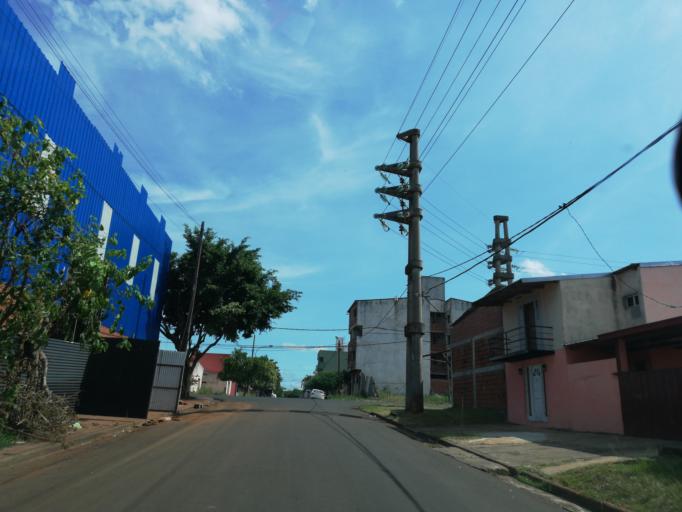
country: AR
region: Misiones
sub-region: Departamento de Capital
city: Posadas
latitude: -27.3762
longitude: -55.8893
